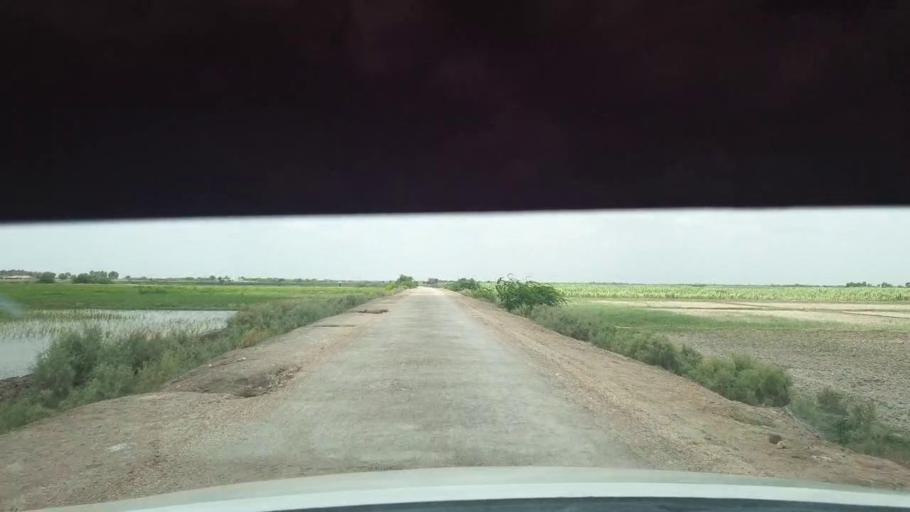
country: PK
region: Sindh
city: Kadhan
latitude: 24.5443
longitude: 69.1253
